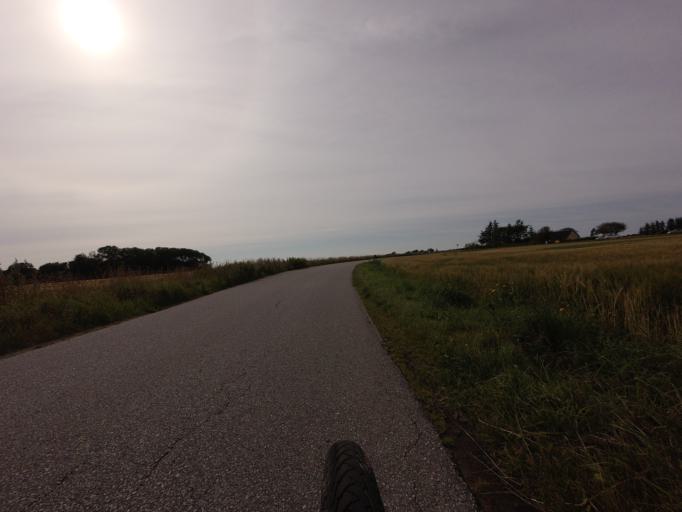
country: DK
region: North Denmark
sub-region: Hjorring Kommune
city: Hjorring
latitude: 57.4353
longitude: 9.8723
